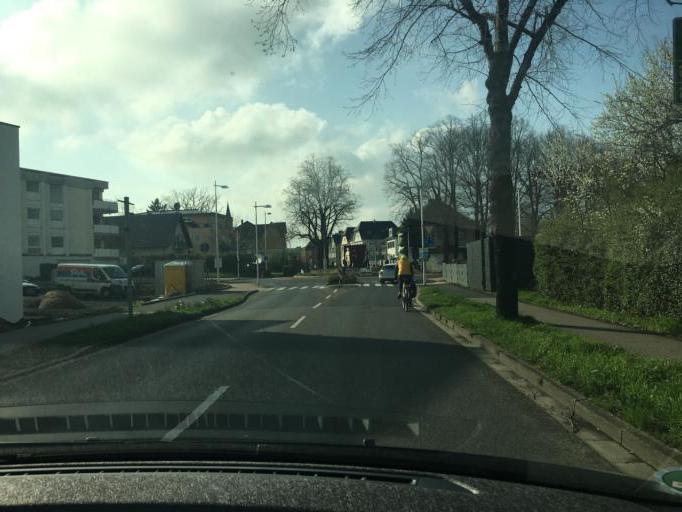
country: DE
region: North Rhine-Westphalia
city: Bornheim
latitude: 50.7601
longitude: 6.9989
